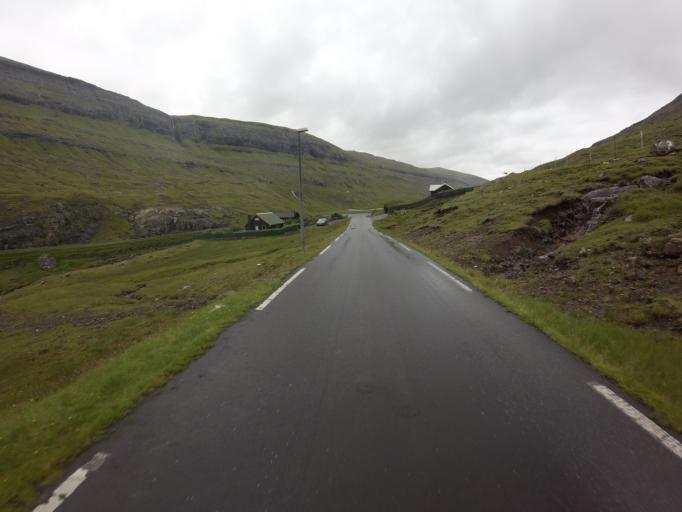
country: FO
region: Streymoy
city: Vestmanna
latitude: 62.2419
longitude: -7.1639
